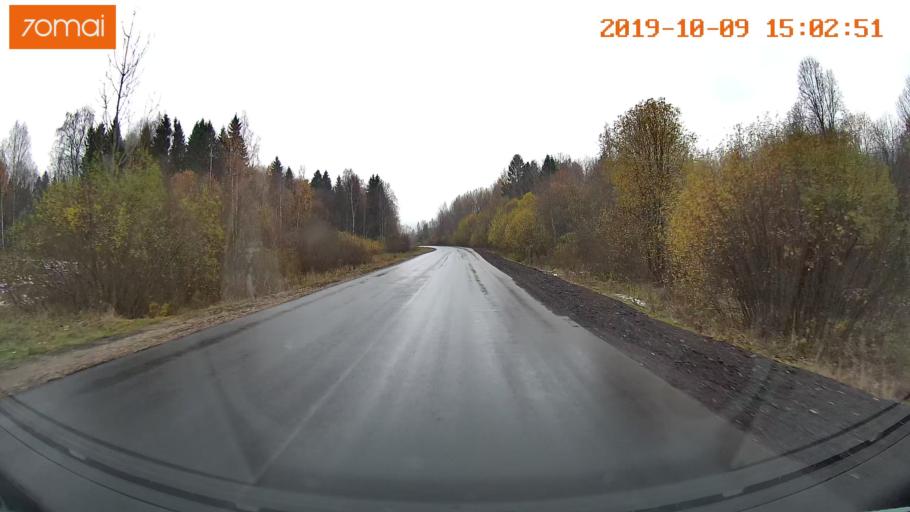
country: RU
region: Kostroma
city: Chistyye Bory
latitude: 58.2791
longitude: 41.6772
